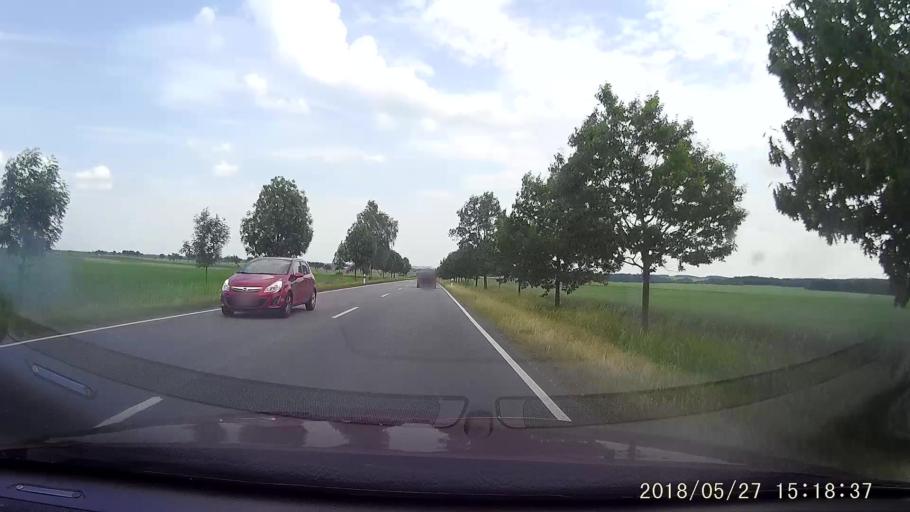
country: DE
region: Saxony
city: Kodersdorf
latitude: 51.2640
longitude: 14.8593
